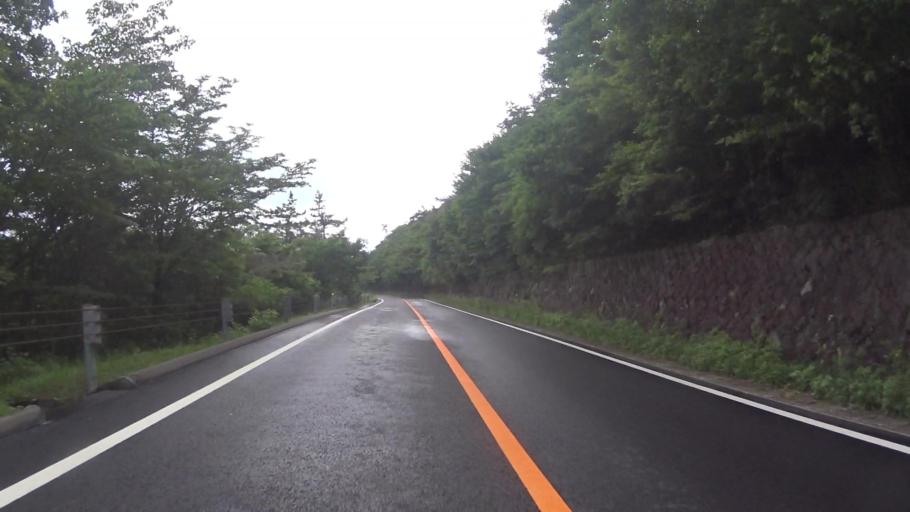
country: JP
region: Oita
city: Tsukawaki
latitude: 33.0919
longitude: 131.1978
